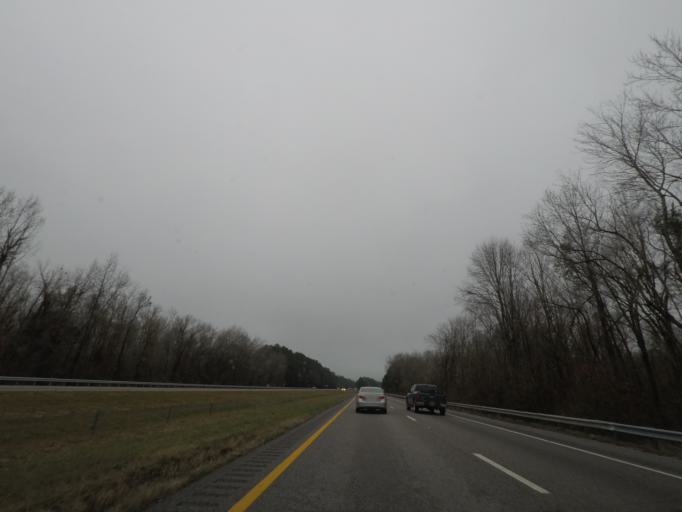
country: US
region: South Carolina
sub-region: Sumter County
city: East Sumter
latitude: 33.9360
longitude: -80.0658
